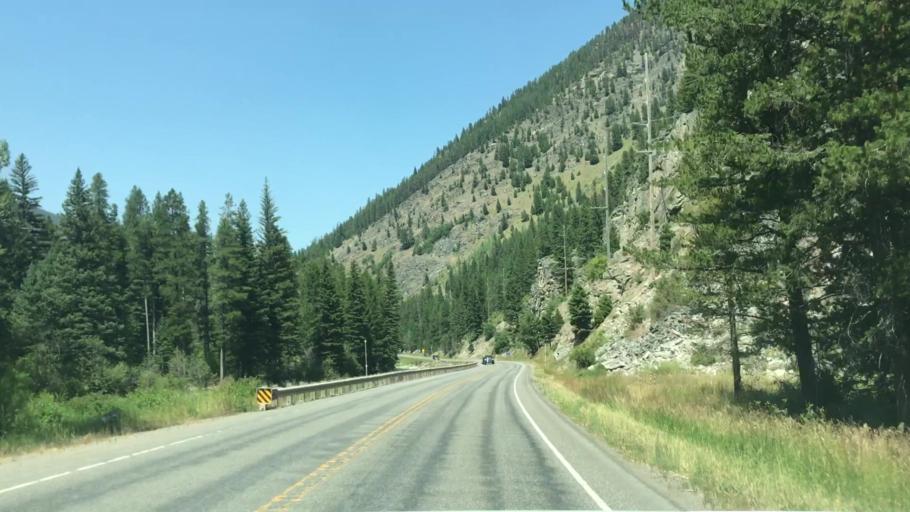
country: US
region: Montana
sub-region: Gallatin County
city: Big Sky
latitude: 45.4015
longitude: -111.2179
